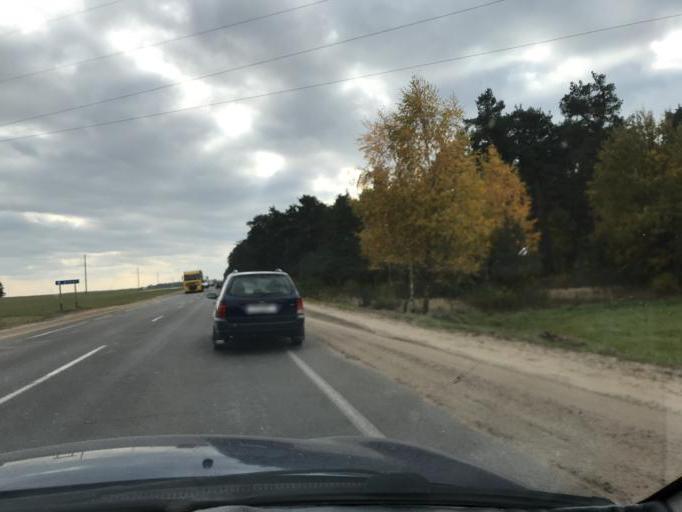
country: BY
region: Grodnenskaya
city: Lida
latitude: 53.8876
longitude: 25.2537
